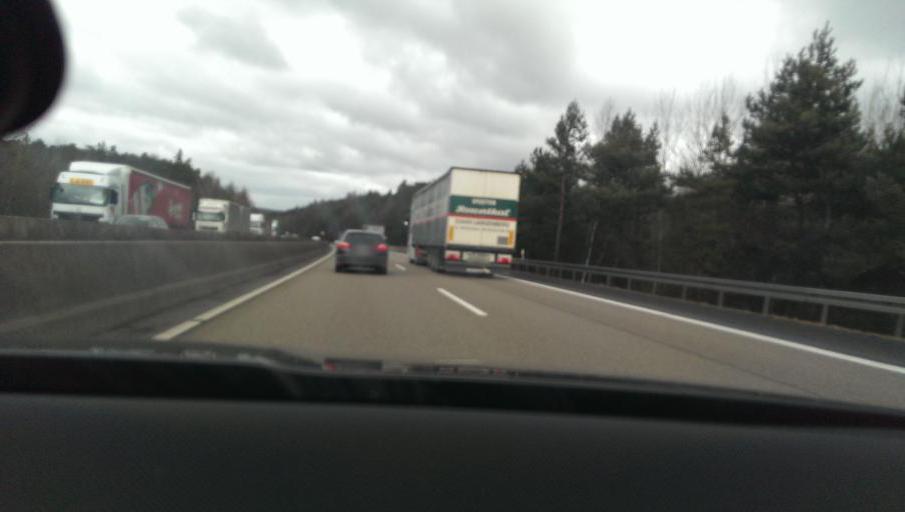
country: DE
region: Hesse
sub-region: Regierungsbezirk Kassel
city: Burghaun
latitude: 50.6419
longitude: 9.6826
